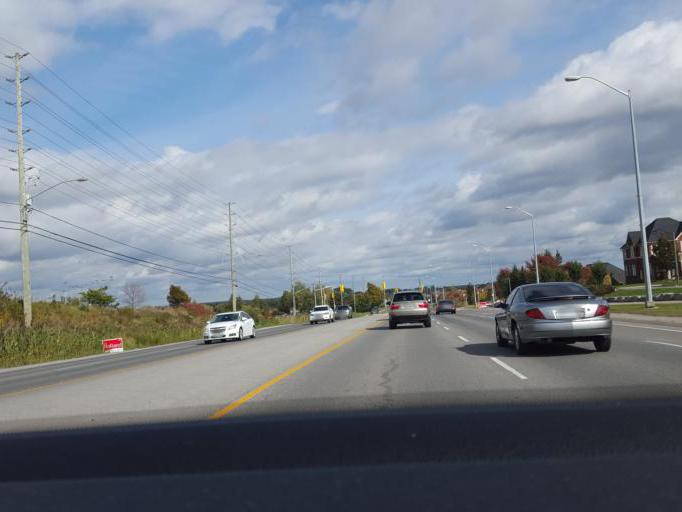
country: CA
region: Ontario
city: Ajax
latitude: 43.8991
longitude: -79.0261
